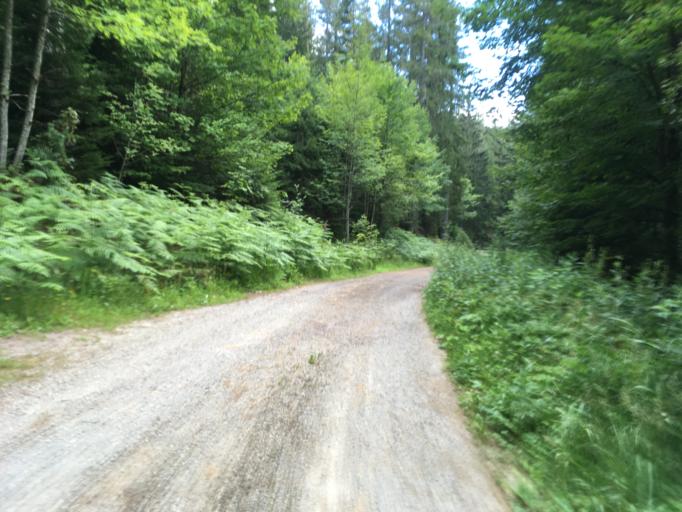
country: DE
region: Baden-Wuerttemberg
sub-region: Karlsruhe Region
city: Baiersbronn
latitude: 48.5642
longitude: 8.4189
